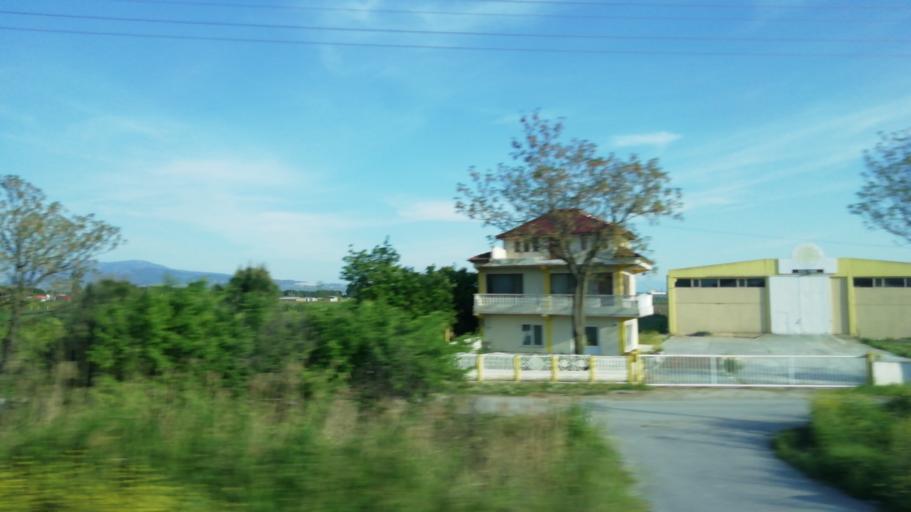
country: TR
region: Manisa
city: Saruhanli
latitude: 38.7282
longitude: 27.5772
